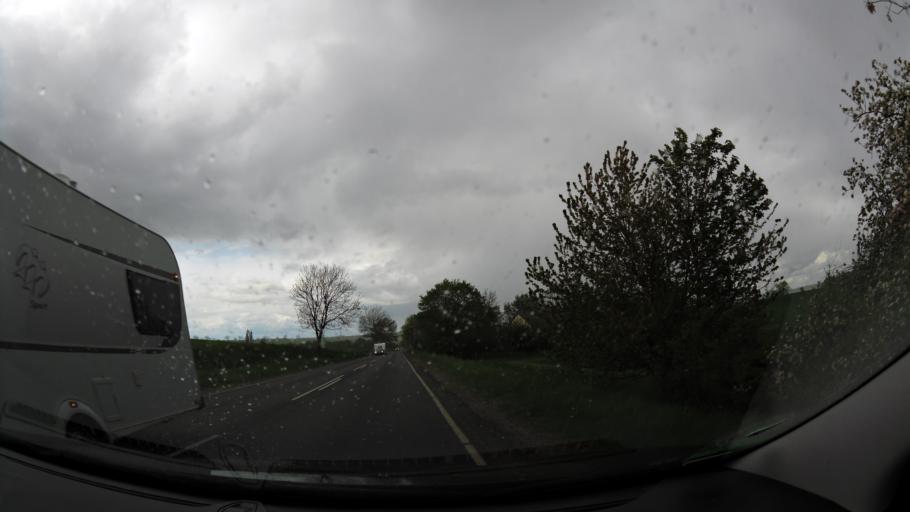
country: DK
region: South Denmark
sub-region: Nyborg Kommune
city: Nyborg
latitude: 55.2754
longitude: 10.7669
